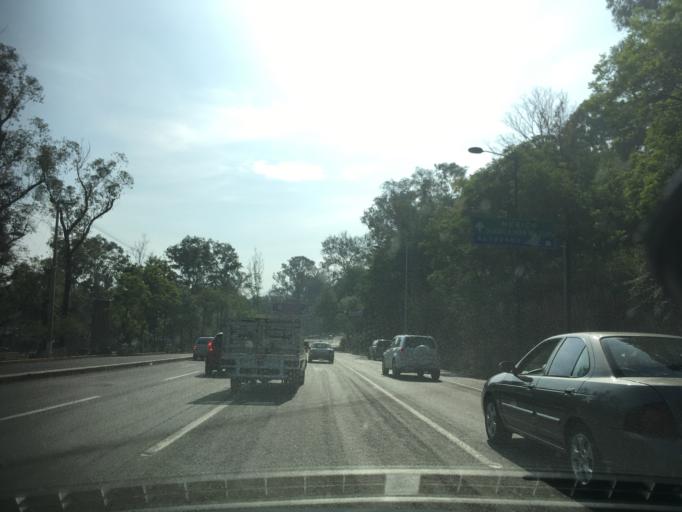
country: MX
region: Michoacan
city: Morelia
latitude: 19.6812
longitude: -101.1965
